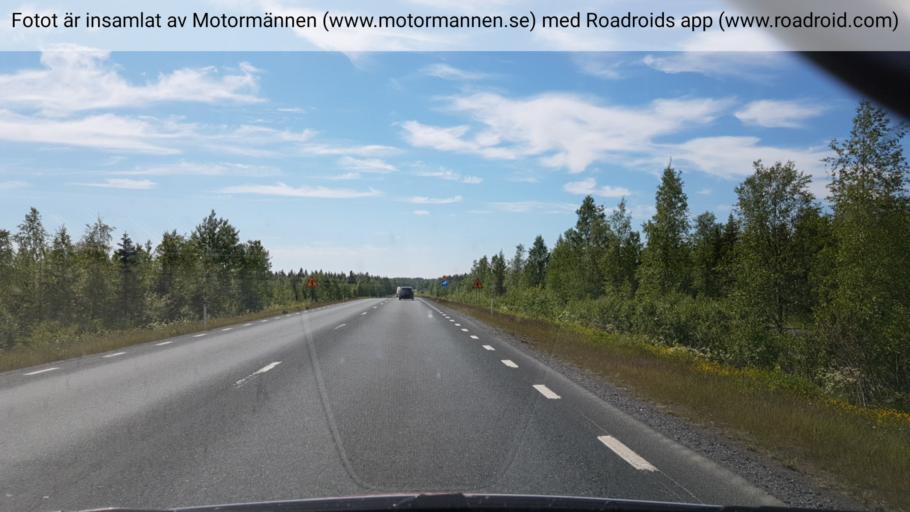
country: SE
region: Norrbotten
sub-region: Haparanda Kommun
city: Haparanda
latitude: 65.8345
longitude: 24.0957
